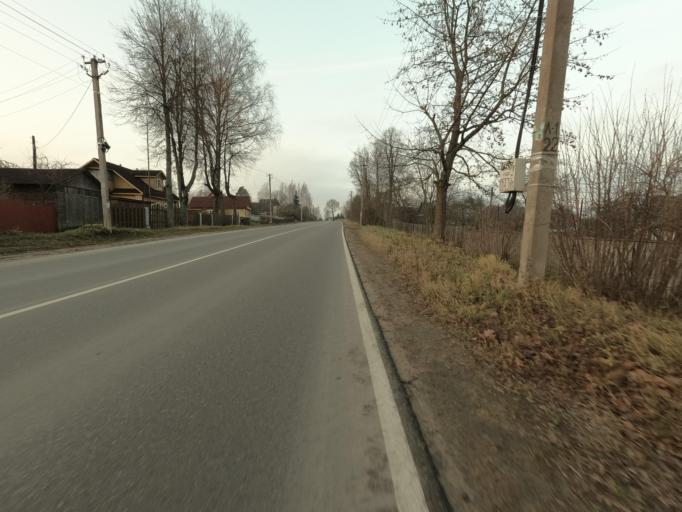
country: RU
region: Leningrad
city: Kirovsk
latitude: 59.8297
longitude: 30.9866
